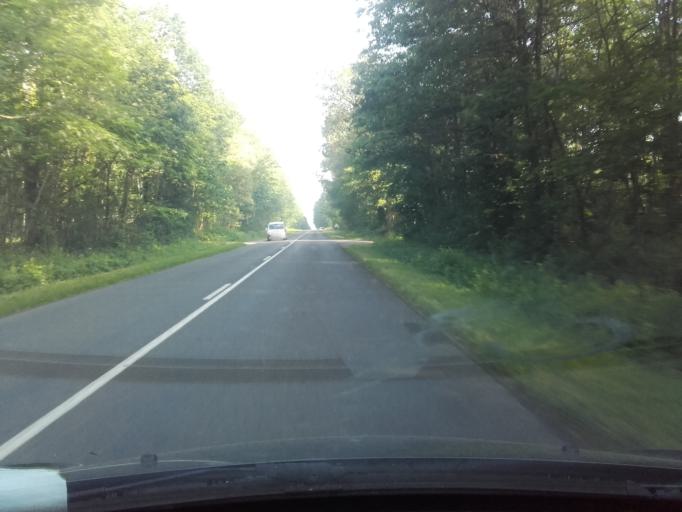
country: FR
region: Centre
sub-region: Departement d'Indre-et-Loire
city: Mazieres-de-Touraine
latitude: 47.3720
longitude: 0.4315
